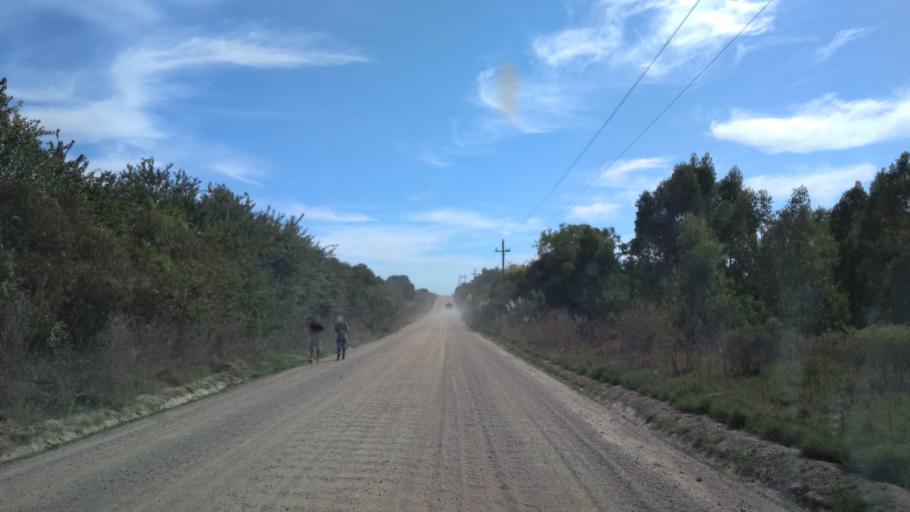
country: UY
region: Canelones
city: Joaquin Suarez
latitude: -34.7152
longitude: -56.0251
